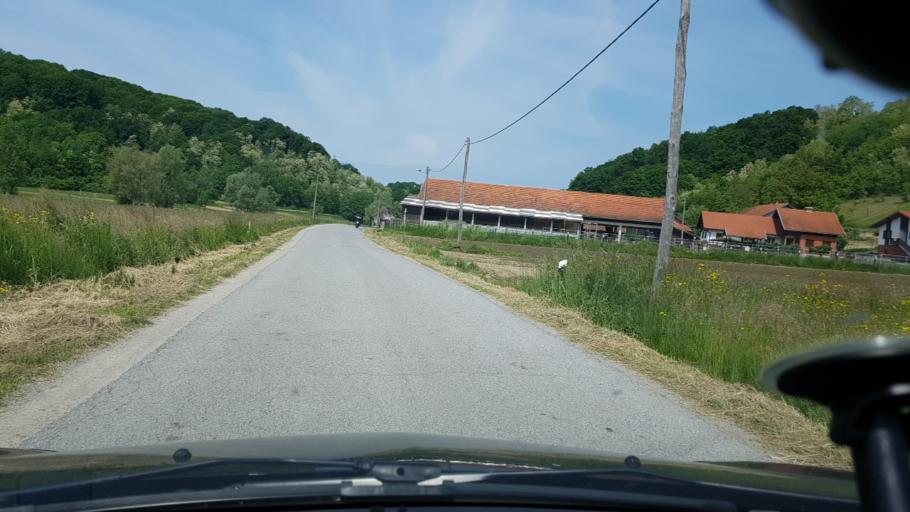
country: HR
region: Krapinsko-Zagorska
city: Selnica
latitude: 46.0291
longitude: 16.0373
